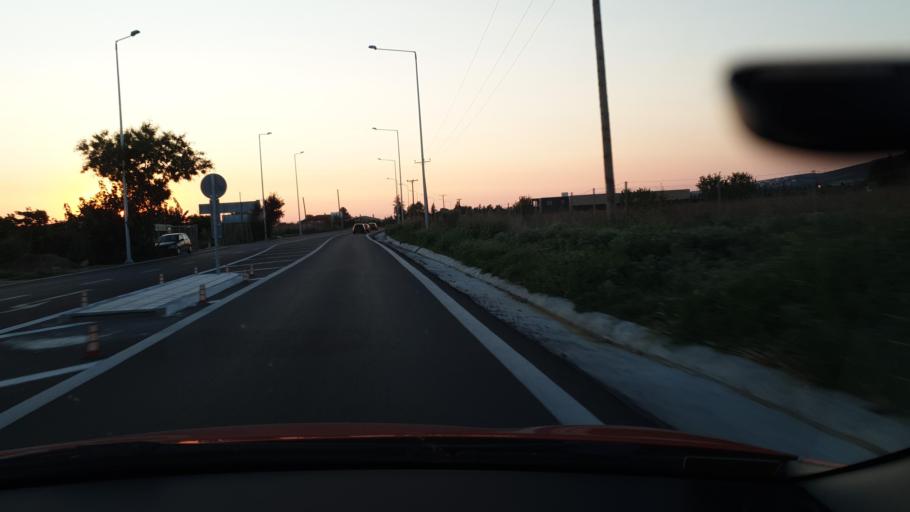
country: GR
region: Central Macedonia
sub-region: Nomos Thessalonikis
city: Souroti
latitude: 40.5017
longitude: 23.0970
